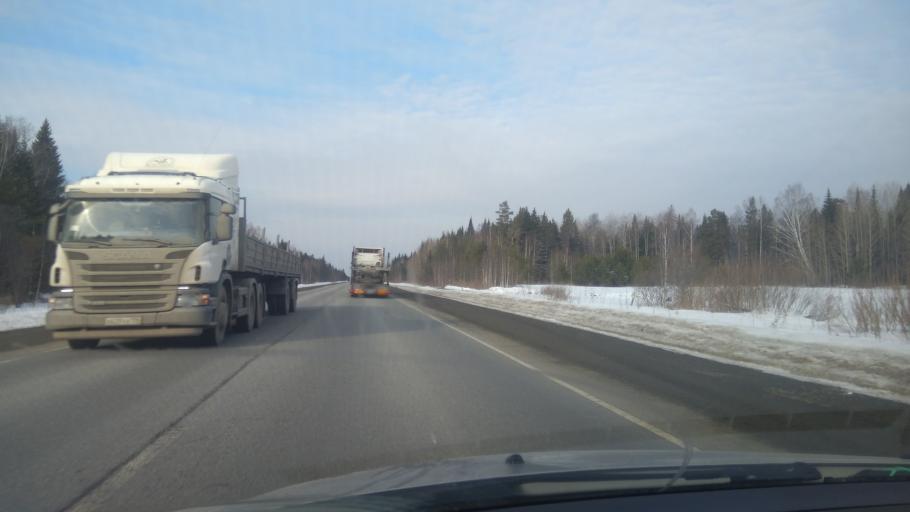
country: RU
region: Sverdlovsk
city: Druzhinino
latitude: 56.7972
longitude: 59.4459
